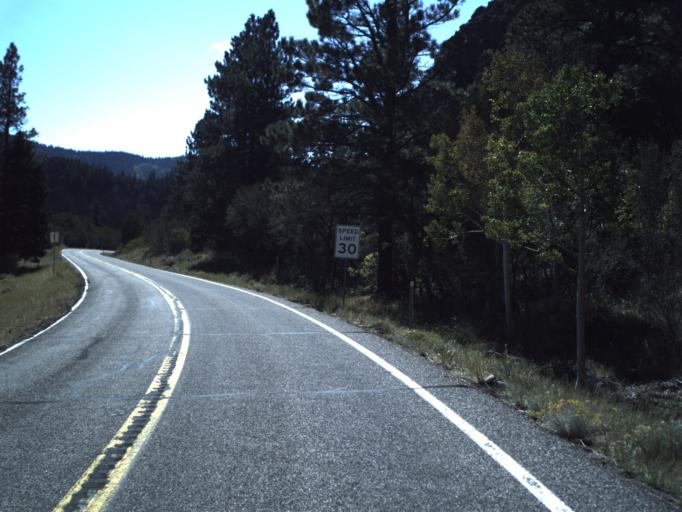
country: US
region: Utah
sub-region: Beaver County
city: Beaver
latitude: 38.2732
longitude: -112.4679
